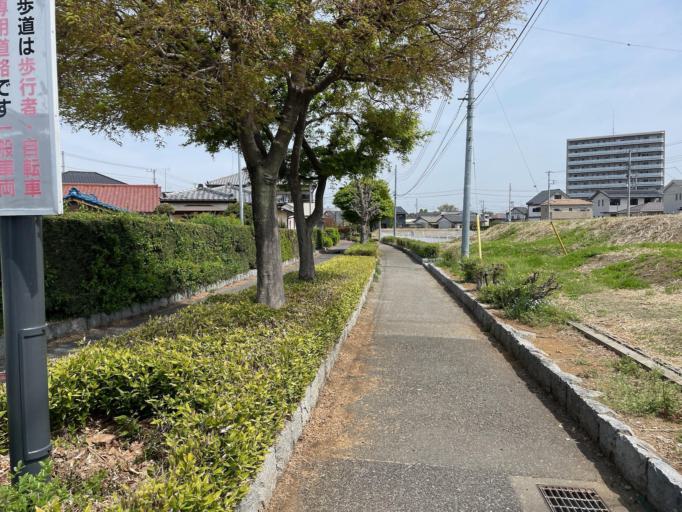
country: JP
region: Saitama
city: Fukayacho
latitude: 36.1932
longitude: 139.2920
